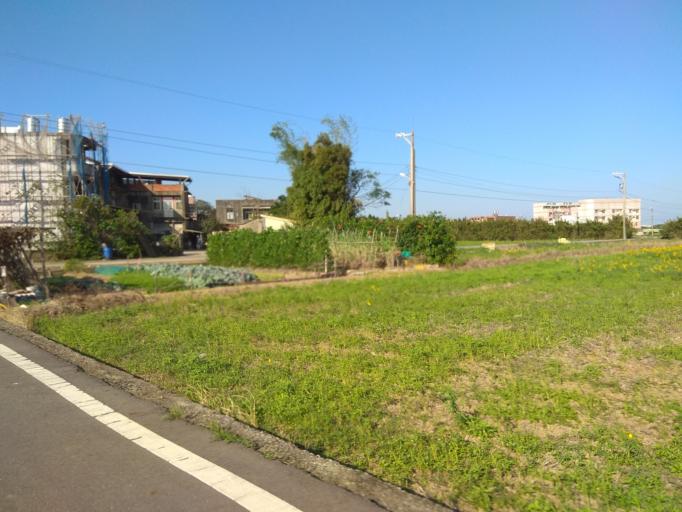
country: TW
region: Taiwan
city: Taoyuan City
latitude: 25.0436
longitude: 121.2243
